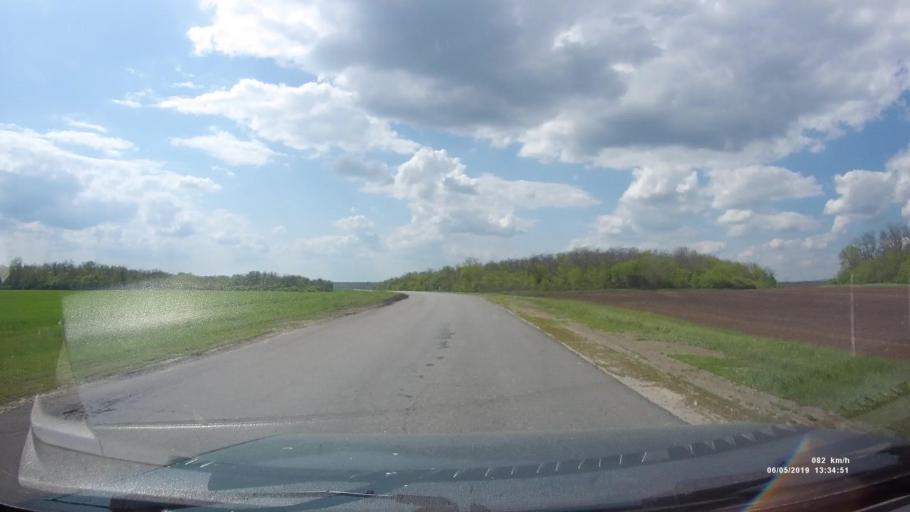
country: RU
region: Rostov
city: Ust'-Donetskiy
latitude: 47.6936
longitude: 40.7562
